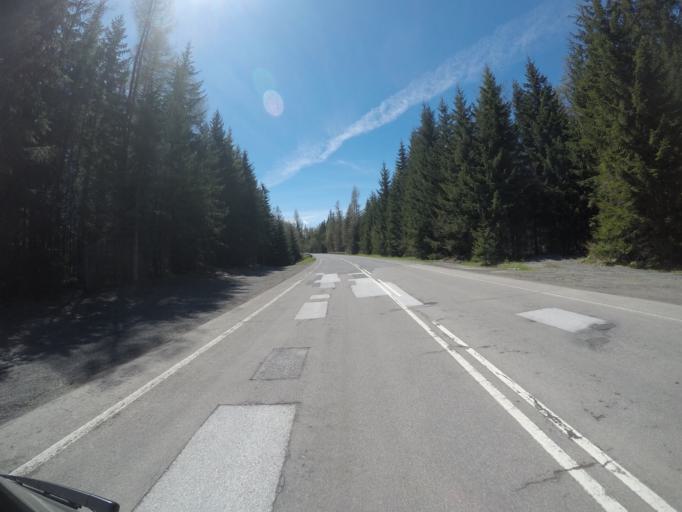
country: SK
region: Presovsky
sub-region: Okres Poprad
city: Strba
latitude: 49.1156
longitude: 20.0804
